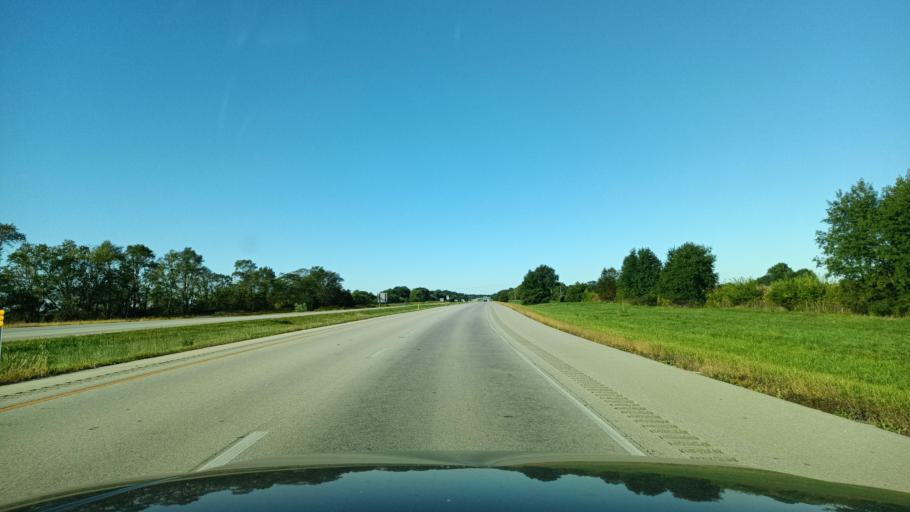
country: US
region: Illinois
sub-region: Knox County
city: Galesburg
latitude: 40.9351
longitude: -90.4149
